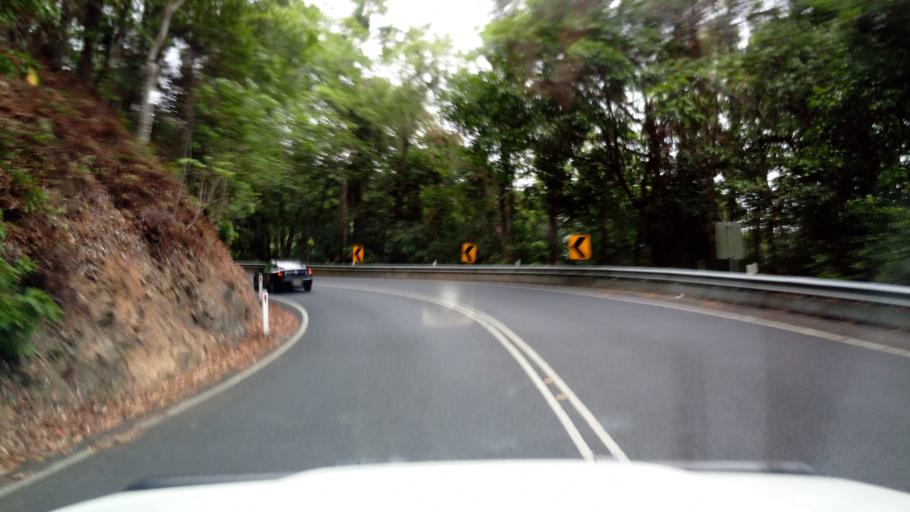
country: AU
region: Queensland
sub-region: Cairns
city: Redlynch
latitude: -16.8471
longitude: 145.6761
